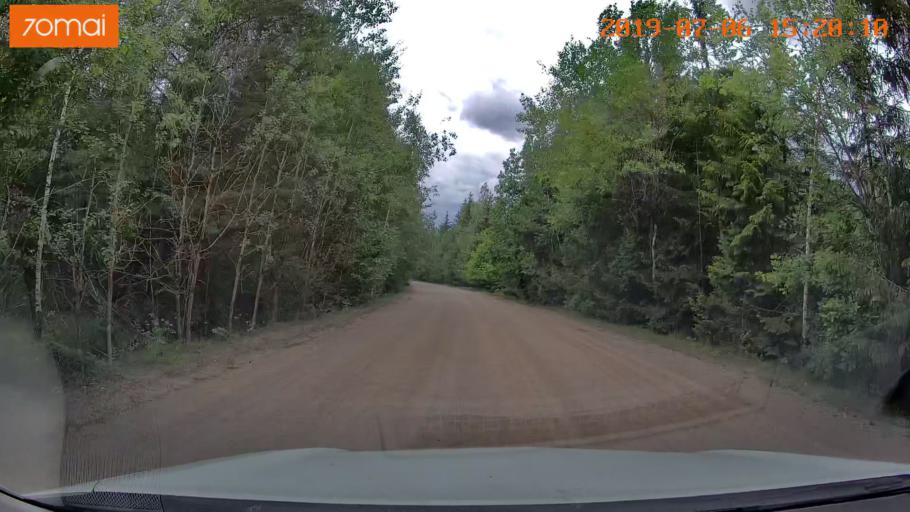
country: BY
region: Minsk
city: Valozhyn
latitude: 54.0046
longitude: 26.6401
